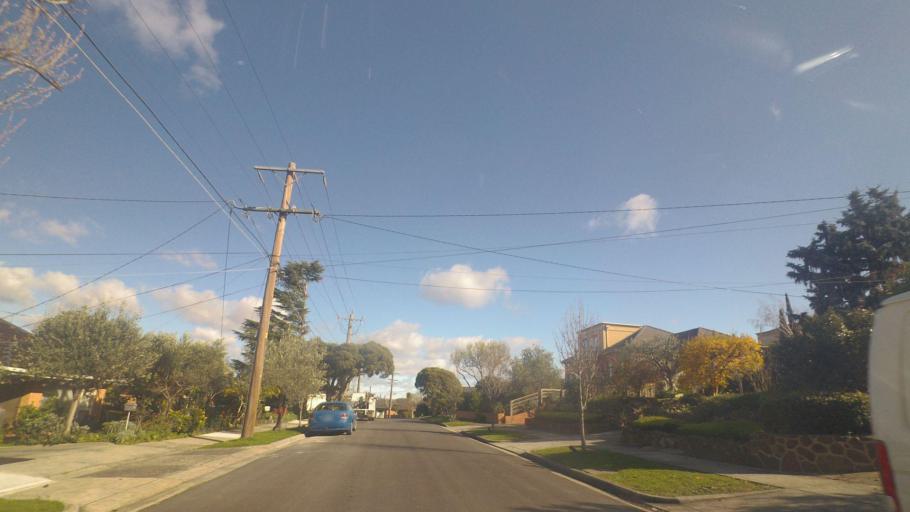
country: AU
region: Victoria
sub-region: Manningham
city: Bulleen
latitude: -37.7773
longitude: 145.0912
